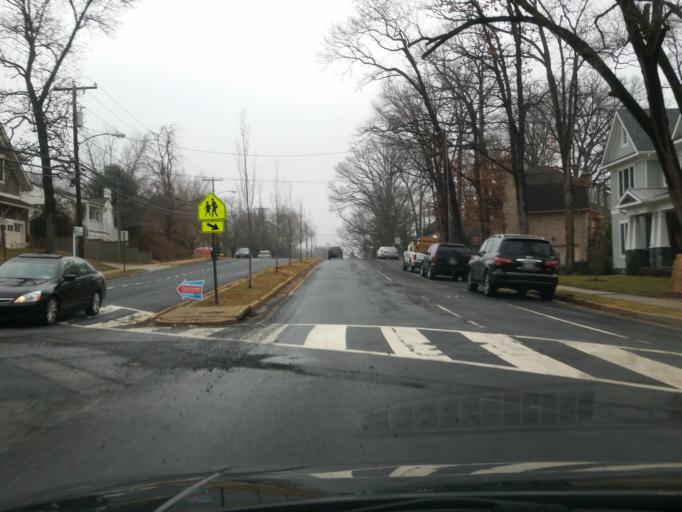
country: US
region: Virginia
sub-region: City of Falls Church
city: Falls Church
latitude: 38.9037
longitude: -77.1529
